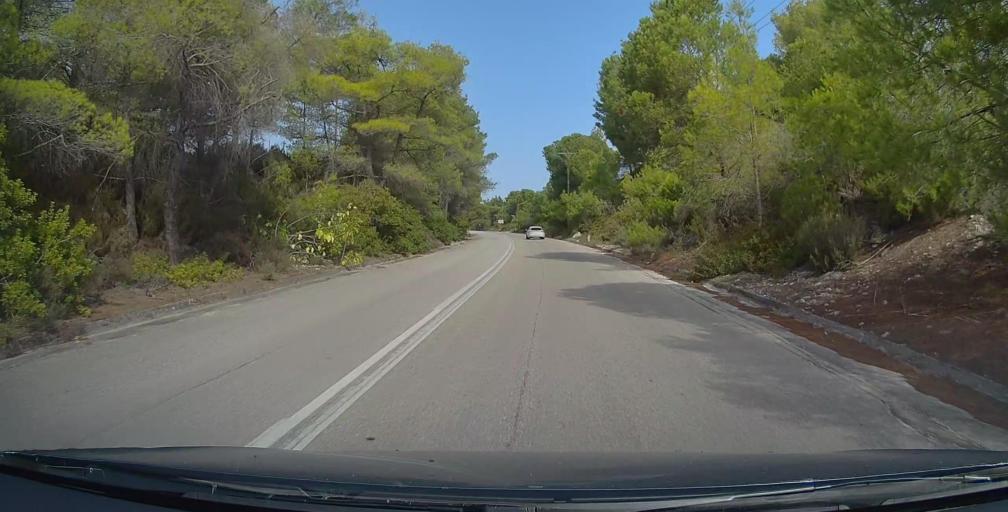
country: GR
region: Central Macedonia
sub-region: Nomos Chalkidikis
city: Sarti
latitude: 40.1219
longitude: 23.9694
